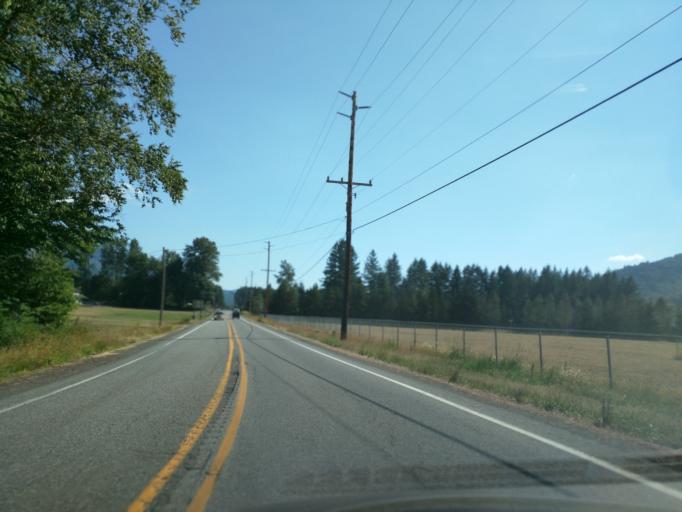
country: US
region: Washington
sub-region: Whatcom County
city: Peaceful Valley
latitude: 48.9161
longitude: -122.1377
